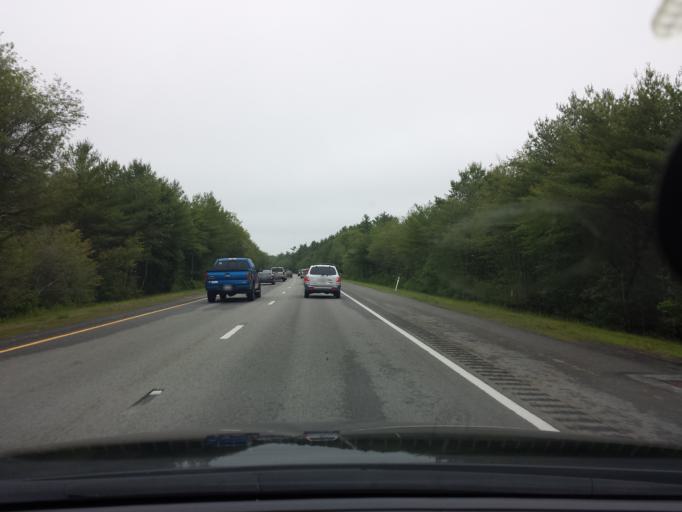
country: US
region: Massachusetts
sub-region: Plymouth County
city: Mattapoisett Center
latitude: 41.6920
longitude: -70.8037
